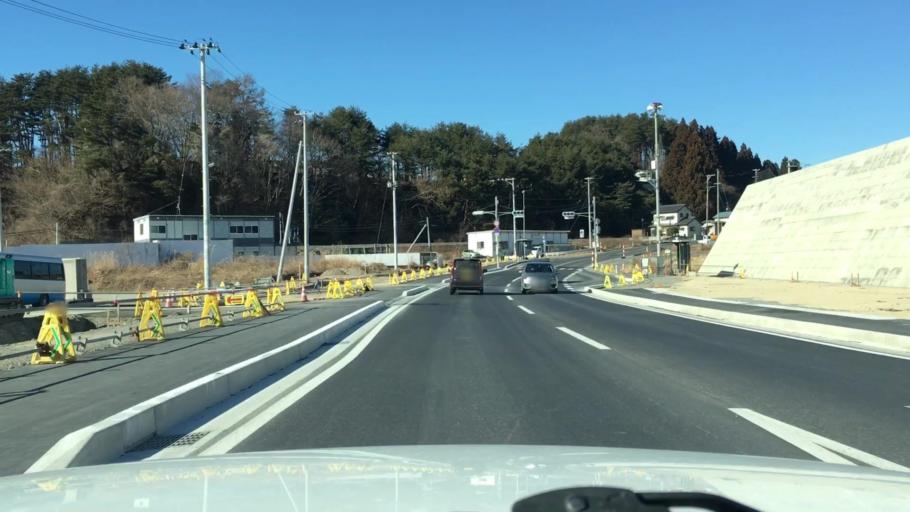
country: JP
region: Iwate
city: Yamada
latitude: 39.4564
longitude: 141.9572
